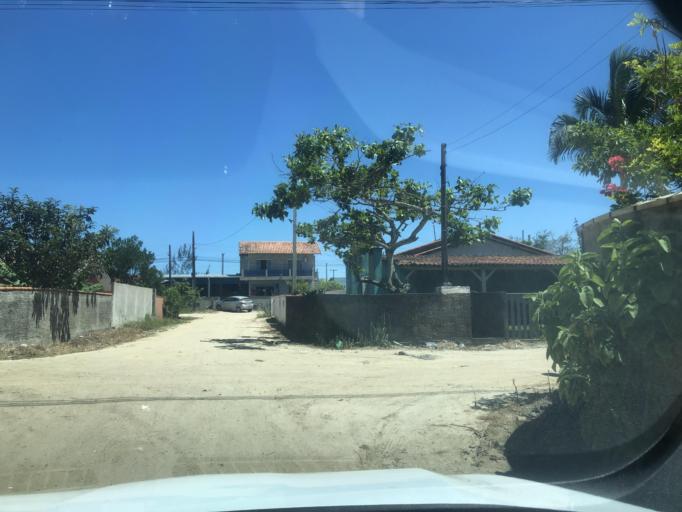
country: BR
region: Santa Catarina
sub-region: Sao Francisco Do Sul
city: Sao Francisco do Sul
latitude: -26.2257
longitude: -48.5243
